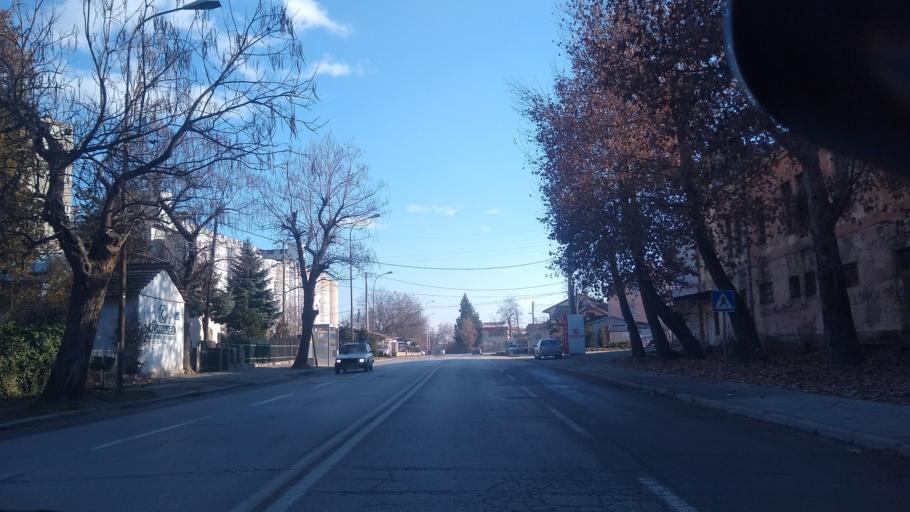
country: MK
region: Bitola
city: Bitola
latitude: 41.0163
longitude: 21.3433
